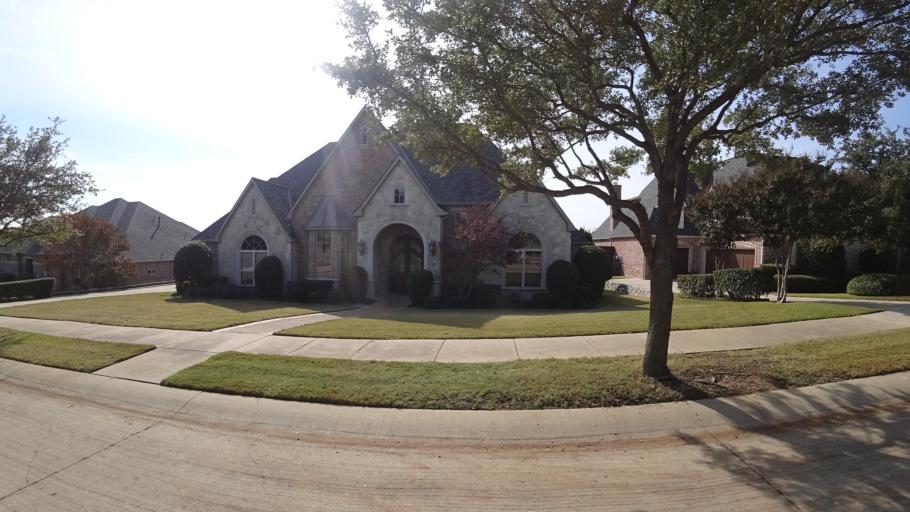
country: US
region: Texas
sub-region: Denton County
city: The Colony
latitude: 33.0382
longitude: -96.8977
